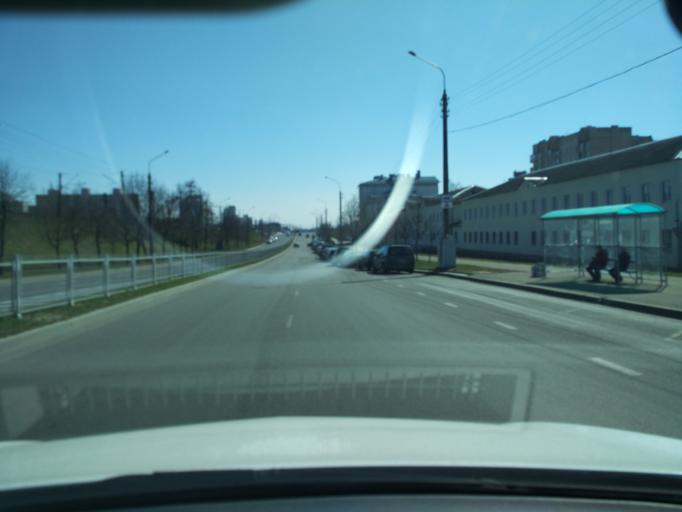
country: BY
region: Minsk
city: Minsk
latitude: 53.8766
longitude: 27.5619
